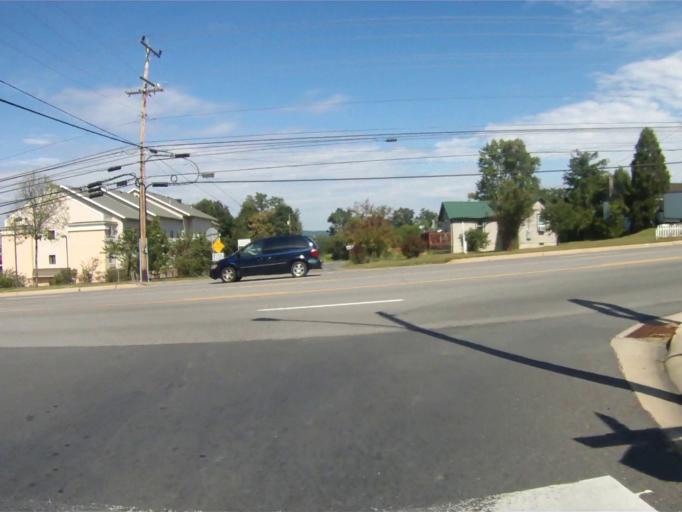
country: US
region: Pennsylvania
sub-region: Centre County
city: Park Forest Village
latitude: 40.8097
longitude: -77.9112
